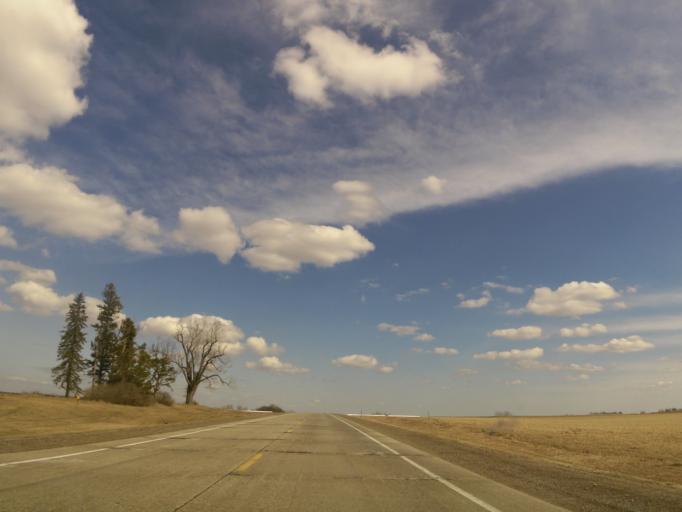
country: US
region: South Dakota
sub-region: Deuel County
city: Clear Lake
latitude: 44.8899
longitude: -96.7586
